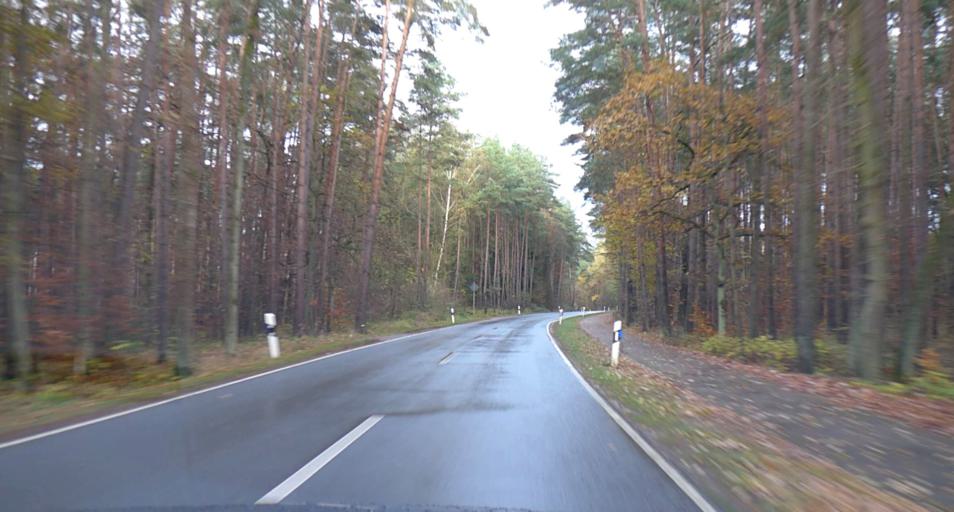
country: DE
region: Bavaria
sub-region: Regierungsbezirk Mittelfranken
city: Marloffstein
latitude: 49.6346
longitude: 11.0470
